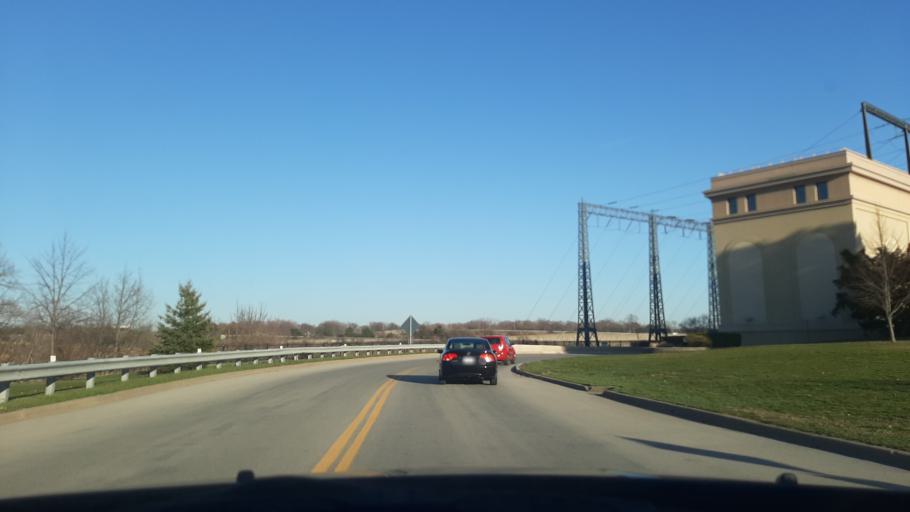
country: US
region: New York
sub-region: Niagara County
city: Lewiston
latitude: 43.1500
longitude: -79.0466
